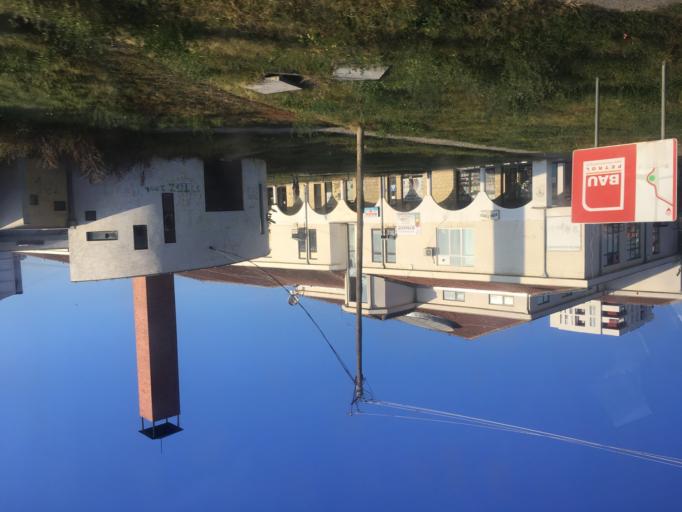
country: XK
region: Pristina
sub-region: Komuna e Drenasit
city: Glogovac
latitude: 42.6203
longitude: 20.8919
